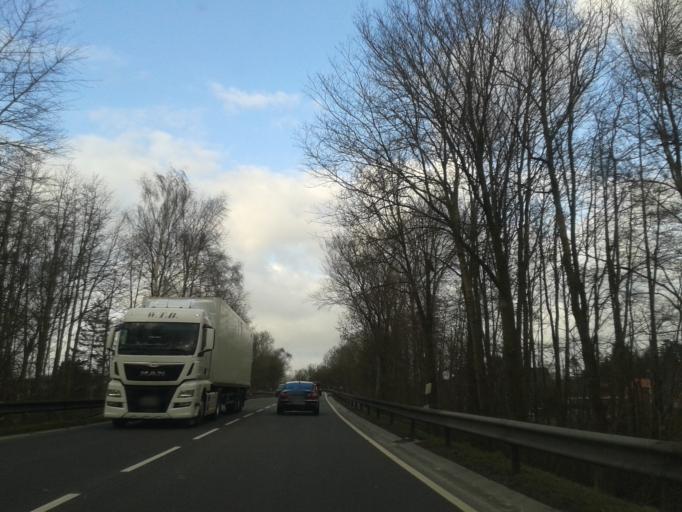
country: DE
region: Lower Saxony
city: Upgant-Schott
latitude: 53.5202
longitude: 7.2806
